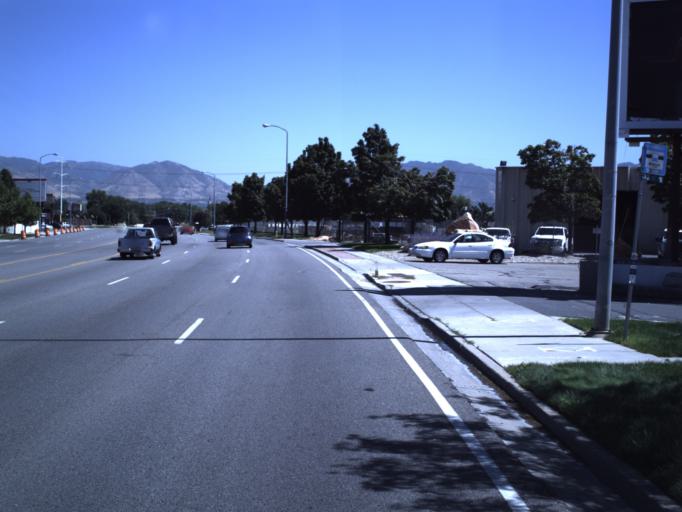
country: US
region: Utah
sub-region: Salt Lake County
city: Taylorsville
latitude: 40.6970
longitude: -111.9344
